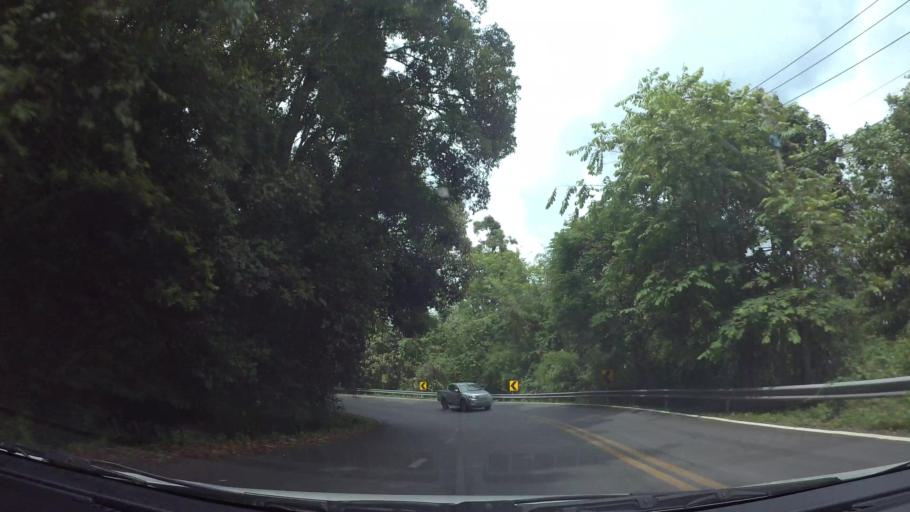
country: TH
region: Chiang Mai
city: Chiang Mai
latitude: 18.7926
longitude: 98.9210
